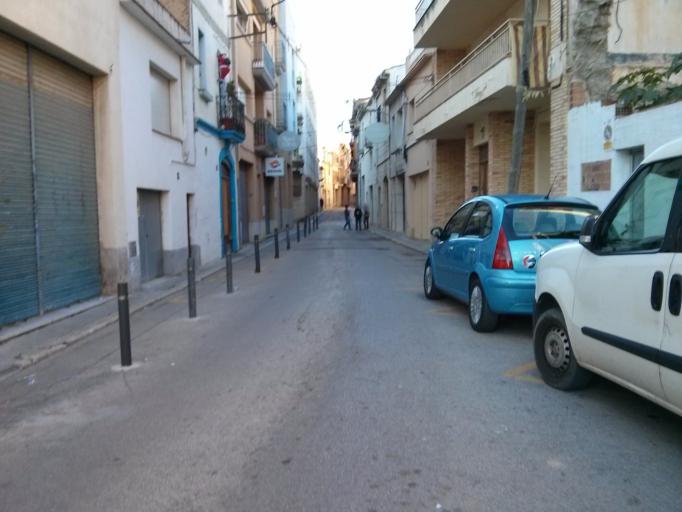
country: ES
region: Catalonia
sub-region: Provincia de Tarragona
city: El Vendrell
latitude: 41.2179
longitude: 1.5351
